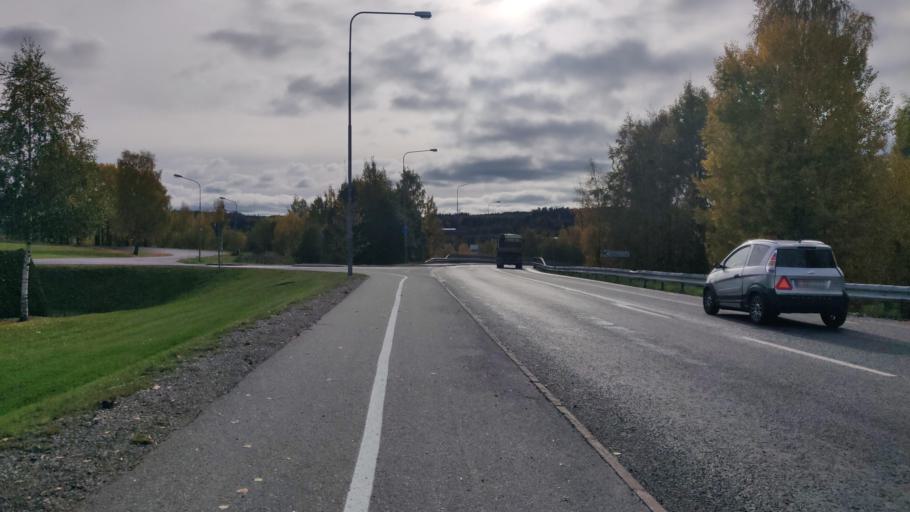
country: SE
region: Vaesternorrland
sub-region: Sundsvalls Kommun
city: Sundsbruk
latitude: 62.4484
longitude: 17.3455
